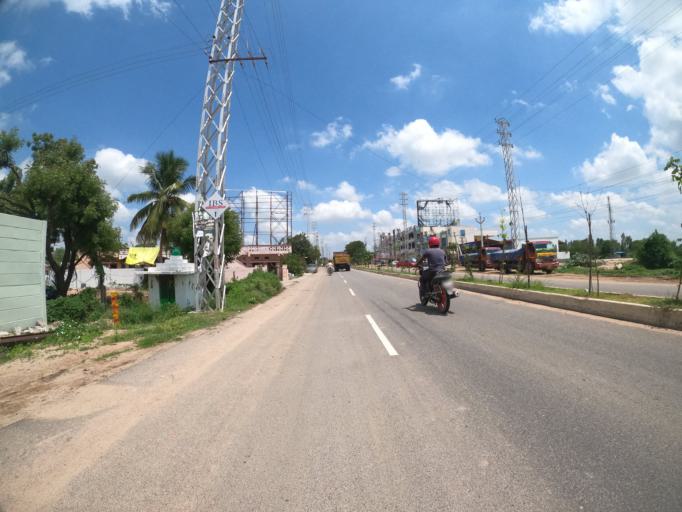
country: IN
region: Telangana
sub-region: Medak
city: Serilingampalle
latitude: 17.4042
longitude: 78.2867
